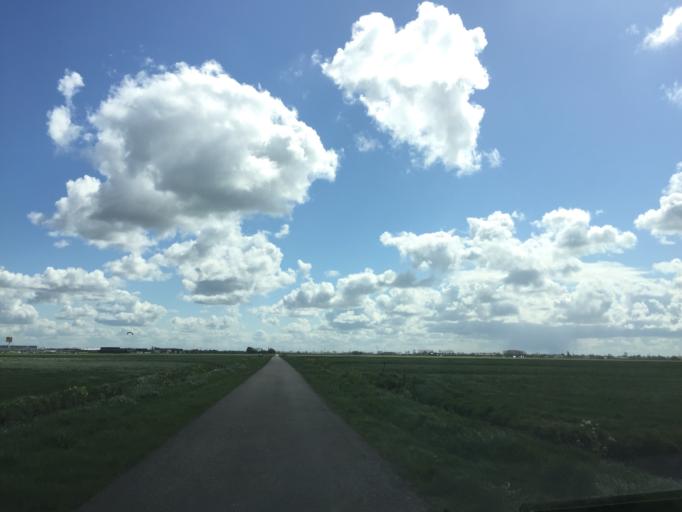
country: NL
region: South Holland
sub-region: Gemeente Kaag en Braassem
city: Oude Wetering
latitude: 52.2099
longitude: 4.6025
